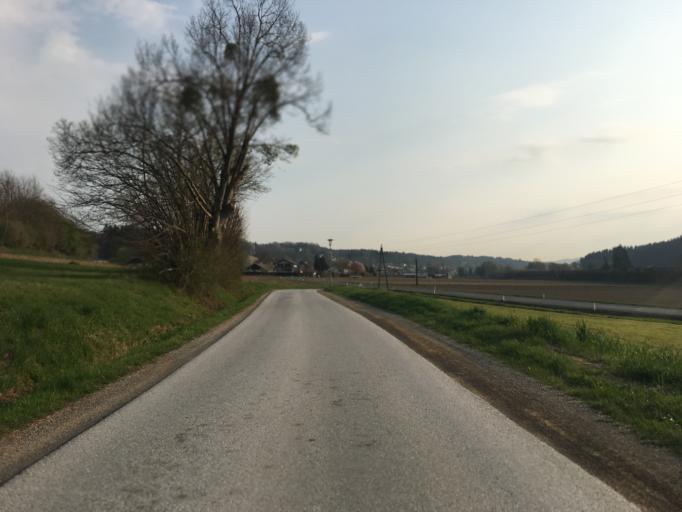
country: AT
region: Styria
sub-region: Politischer Bezirk Weiz
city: Ungerdorf
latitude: 47.0777
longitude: 15.6420
